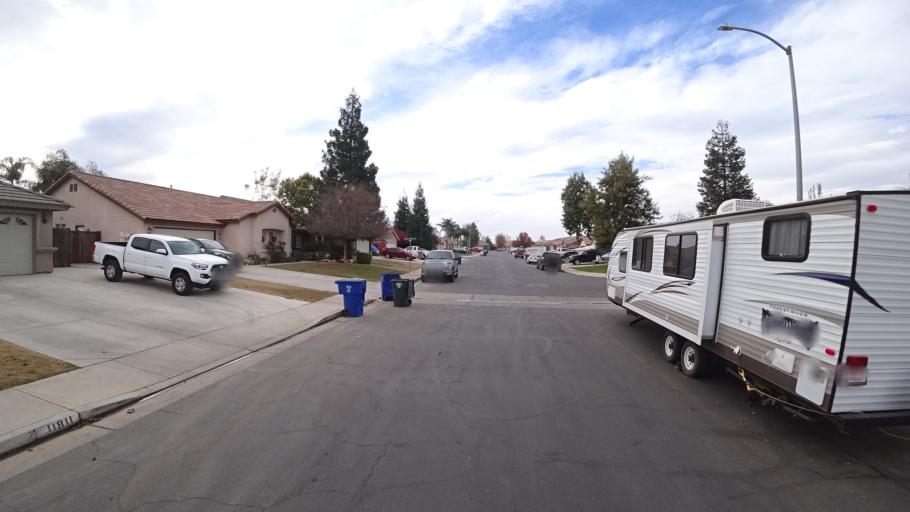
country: US
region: California
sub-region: Kern County
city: Rosedale
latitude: 35.4165
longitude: -119.1337
